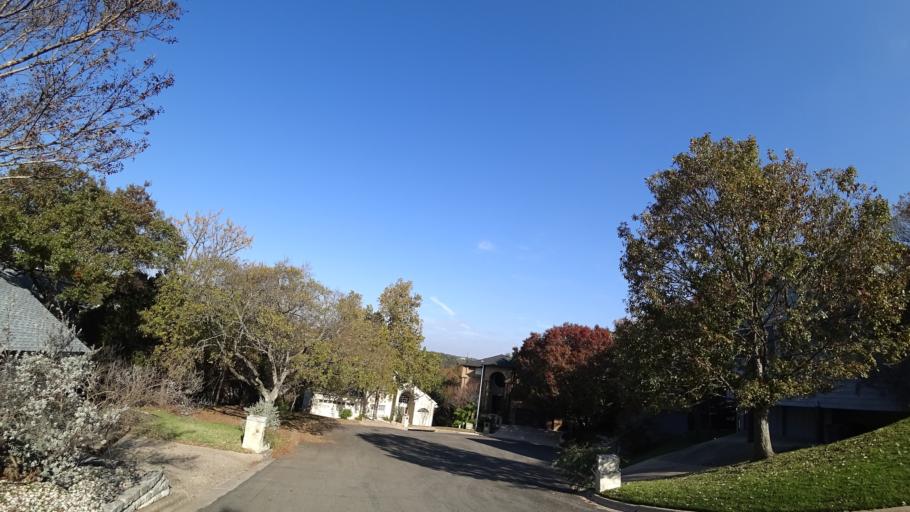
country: US
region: Texas
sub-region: Williamson County
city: Jollyville
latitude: 30.3925
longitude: -97.7627
